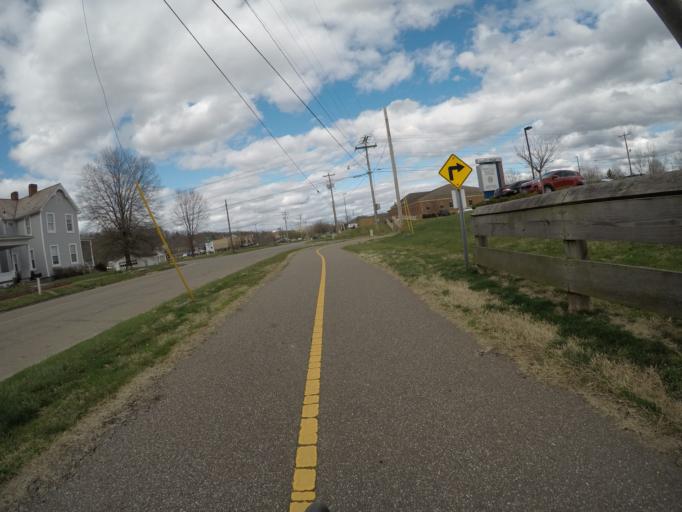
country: US
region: West Virginia
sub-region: Wood County
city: Williamstown
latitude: 39.4120
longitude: -81.4393
